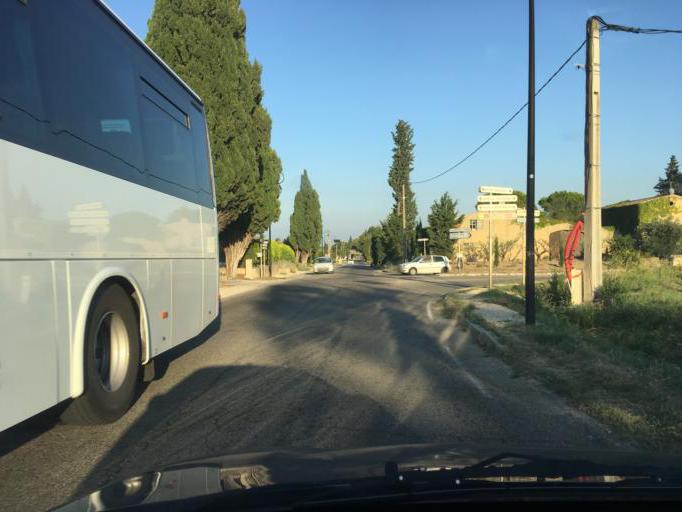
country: FR
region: Languedoc-Roussillon
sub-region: Departement du Gard
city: Tavel
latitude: 44.0106
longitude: 4.7082
